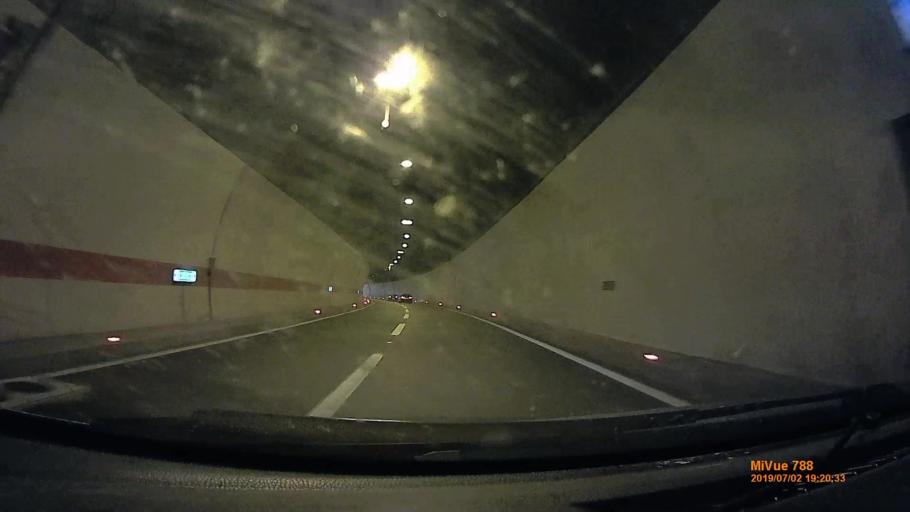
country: HR
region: Varazdinska
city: Ljubescica
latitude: 46.2041
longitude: 16.4123
